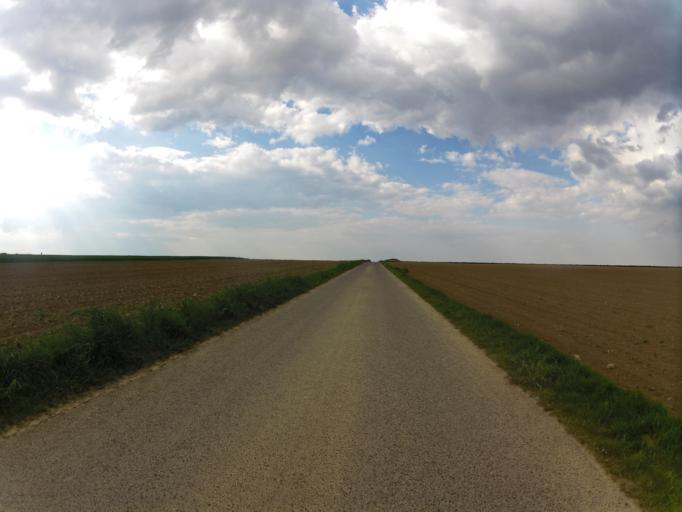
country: DE
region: Bavaria
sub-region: Regierungsbezirk Unterfranken
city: Giebelstadt
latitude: 49.6383
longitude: 9.9389
